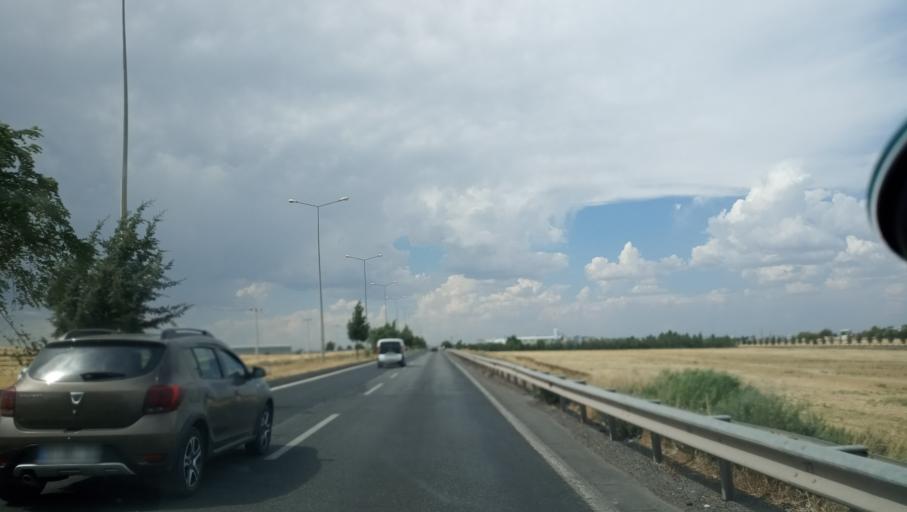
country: TR
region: Diyarbakir
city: Diyarbakir
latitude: 37.8776
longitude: 40.2206
